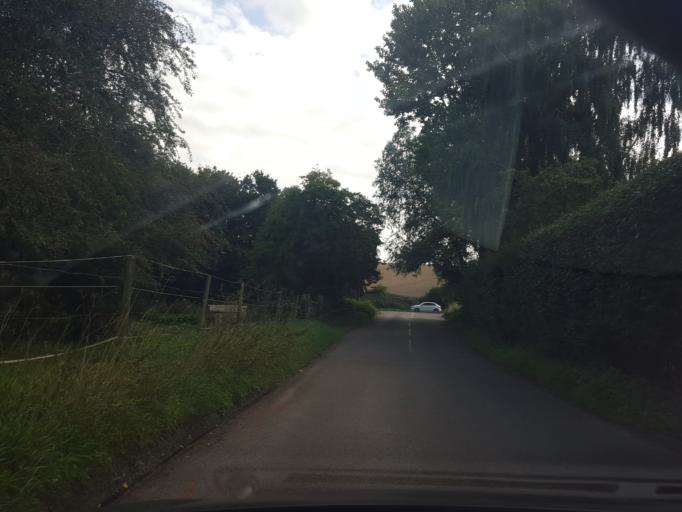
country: GB
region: England
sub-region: Suffolk
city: Shotley Gate
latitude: 51.9261
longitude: 1.2037
